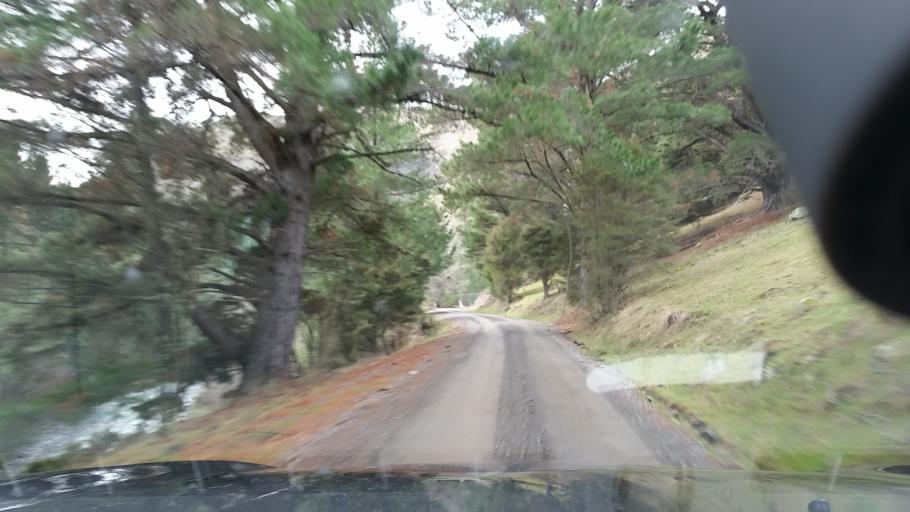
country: NZ
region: Tasman
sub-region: Tasman District
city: Richmond
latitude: -41.7303
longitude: 173.4666
